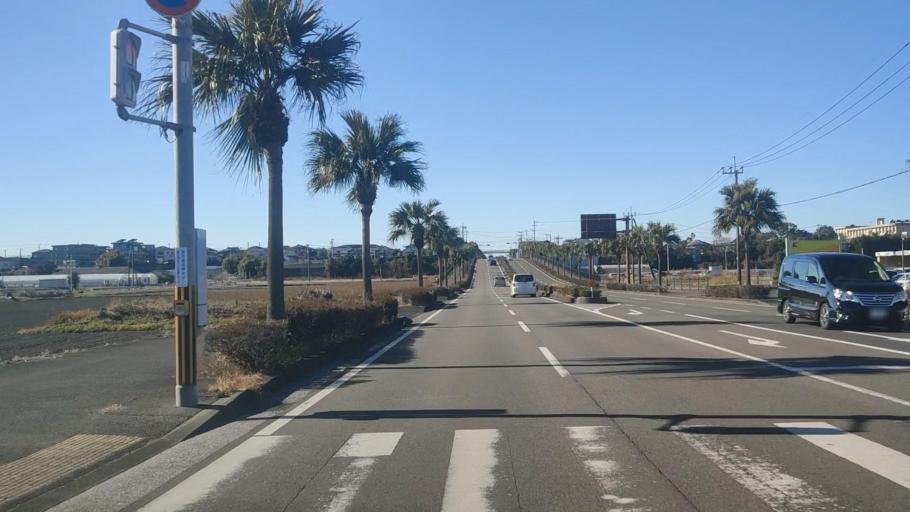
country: JP
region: Miyazaki
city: Miyazaki-shi
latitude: 31.9399
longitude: 131.4547
